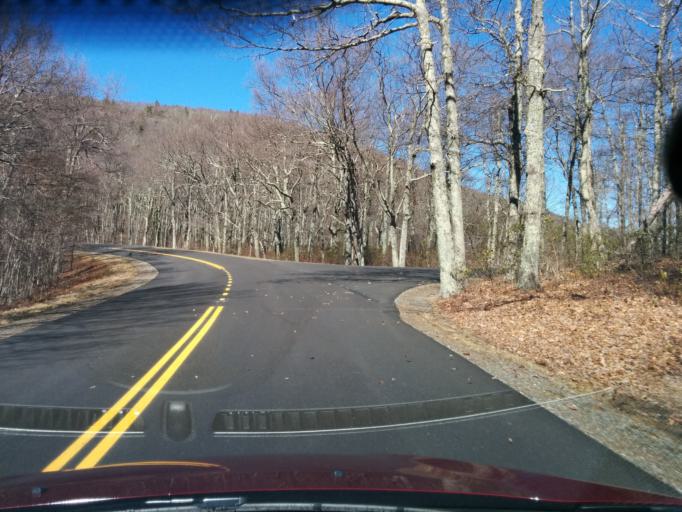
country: US
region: Virginia
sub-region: Augusta County
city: Stuarts Draft
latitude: 37.9073
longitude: -79.0514
